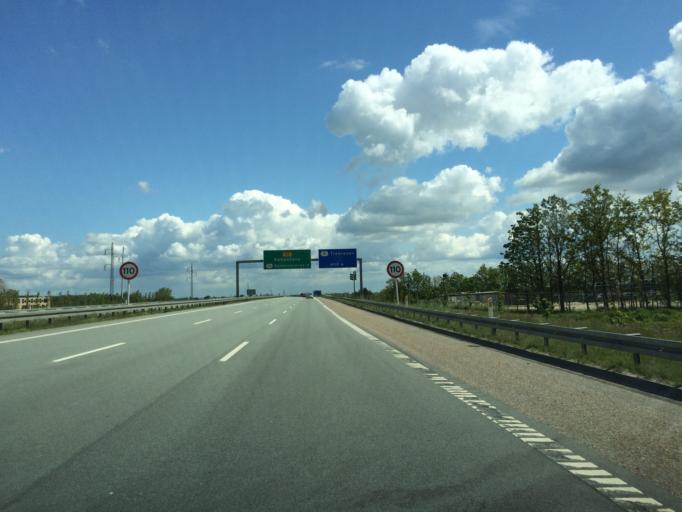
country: DK
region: Zealand
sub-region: Roskilde Kommune
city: Vindinge
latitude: 55.6469
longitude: 12.1387
